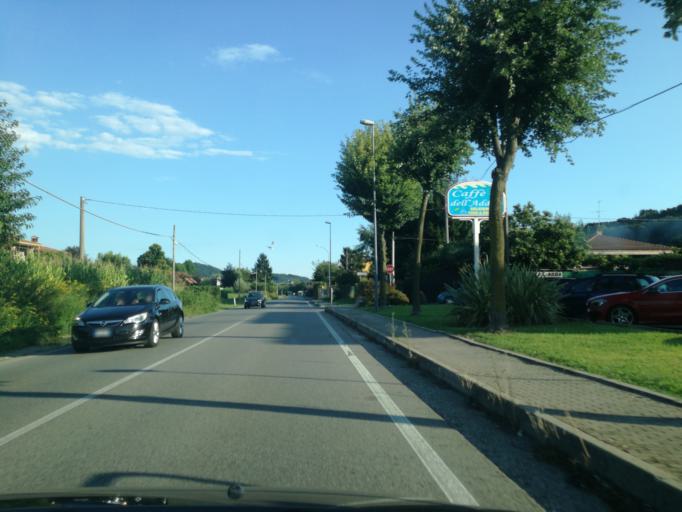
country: IT
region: Lombardy
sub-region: Provincia di Lecco
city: Arlate
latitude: 45.7260
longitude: 9.4425
